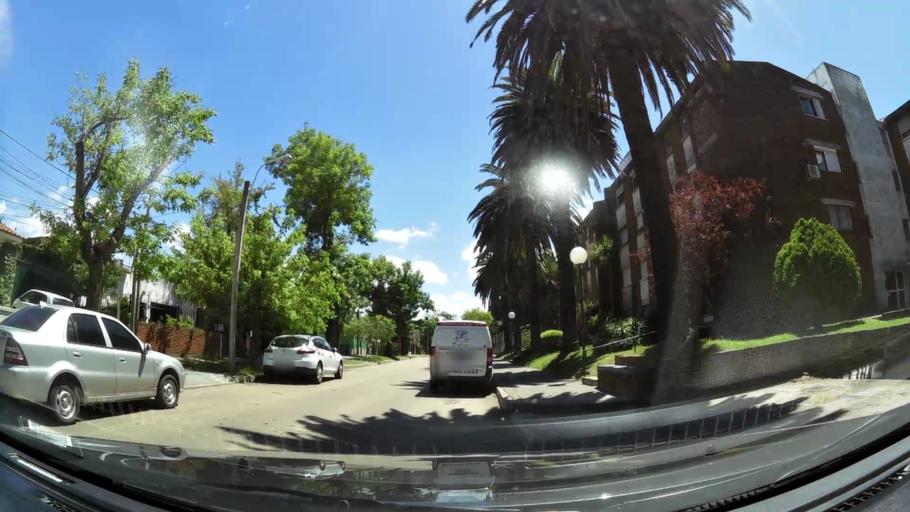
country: UY
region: Montevideo
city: Montevideo
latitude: -34.9019
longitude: -56.1302
